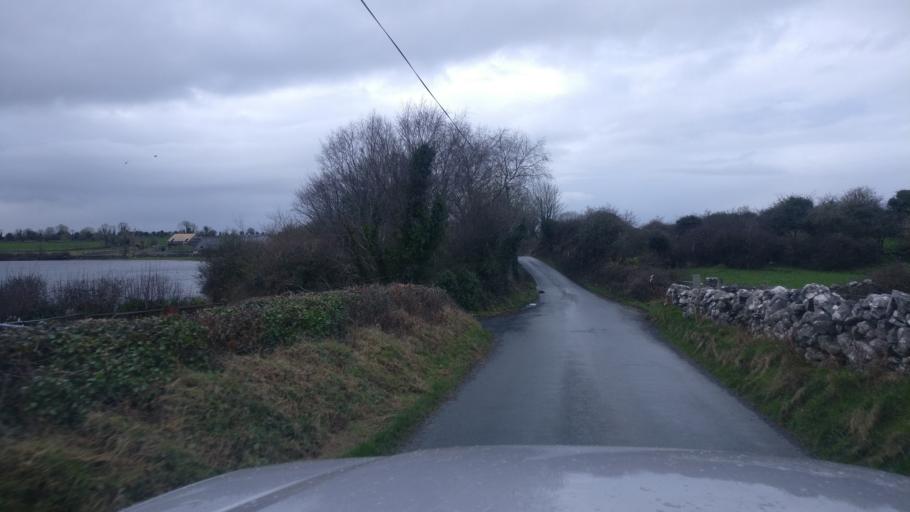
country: IE
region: Connaught
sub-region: County Galway
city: Athenry
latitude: 53.1854
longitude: -8.7098
